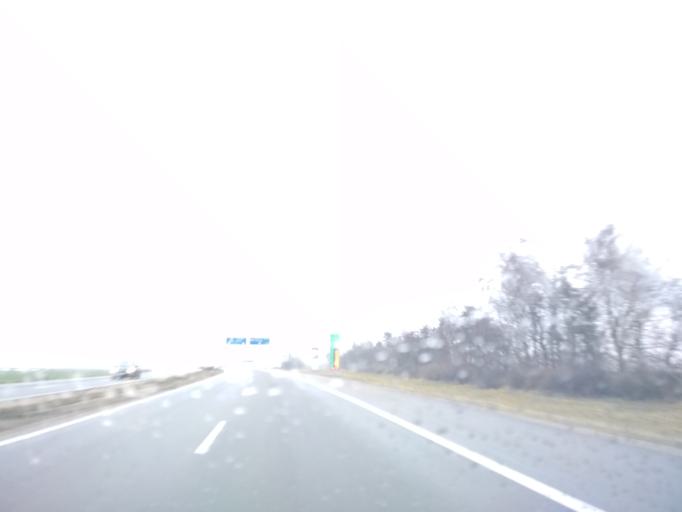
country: BY
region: Minsk
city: Blon'
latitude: 53.5507
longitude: 28.1603
